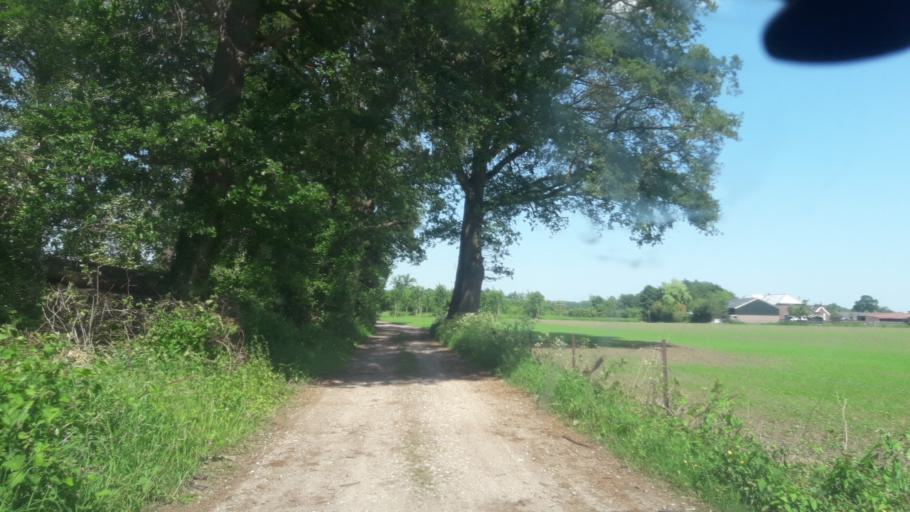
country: NL
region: Overijssel
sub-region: Gemeente Deventer
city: Schalkhaar
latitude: 52.3206
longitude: 6.1971
